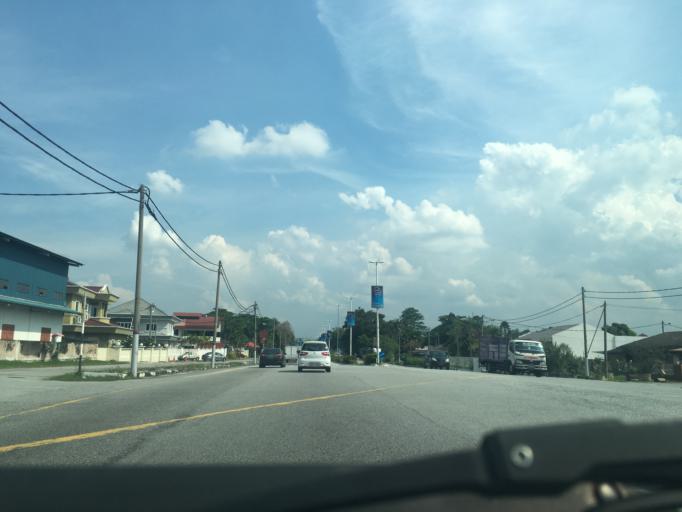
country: MY
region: Perak
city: Ipoh
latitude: 4.6177
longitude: 101.0800
